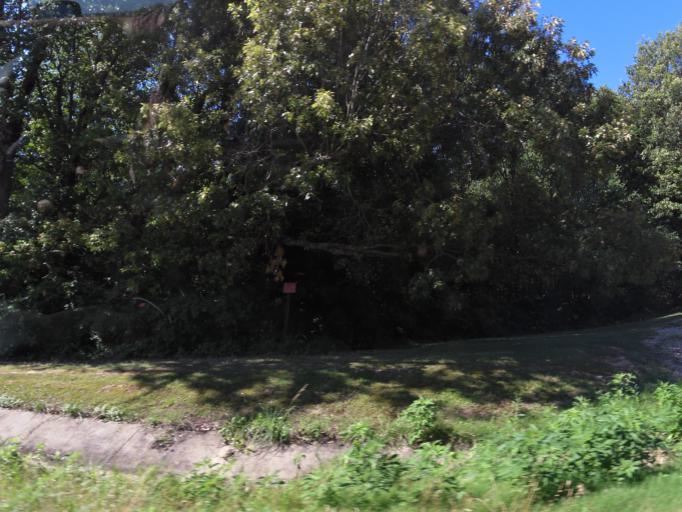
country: US
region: Arkansas
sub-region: Clay County
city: Piggott
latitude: 36.4332
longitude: -90.3030
